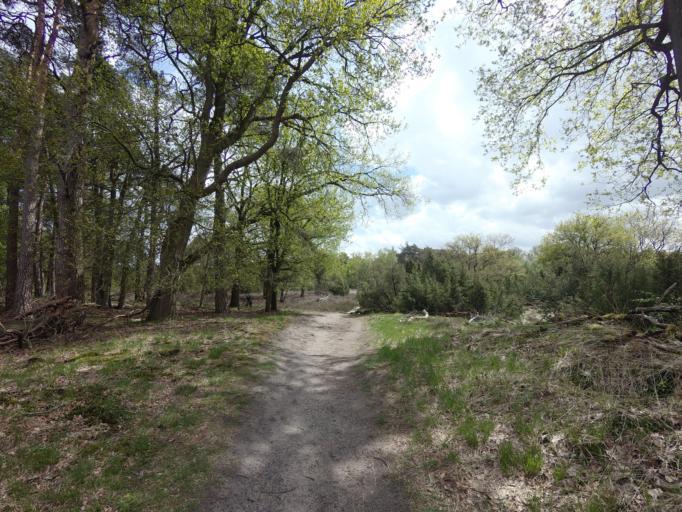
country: NL
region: Overijssel
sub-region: Gemeente Haaksbergen
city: Haaksbergen
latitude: 52.1535
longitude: 6.8029
